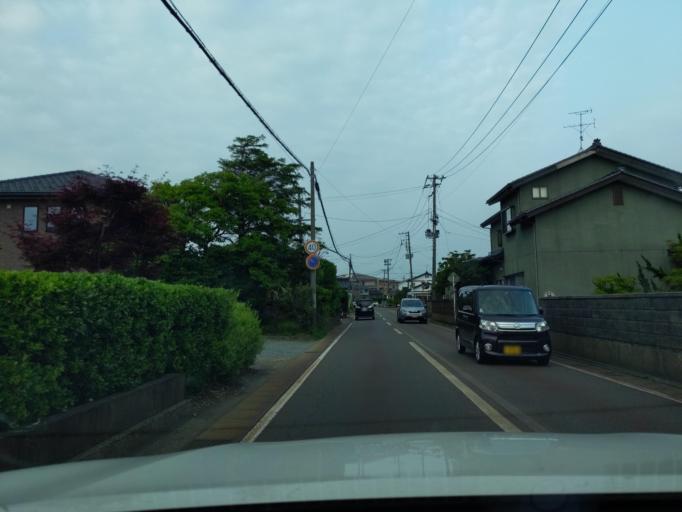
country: JP
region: Niigata
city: Kashiwazaki
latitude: 37.3882
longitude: 138.5834
